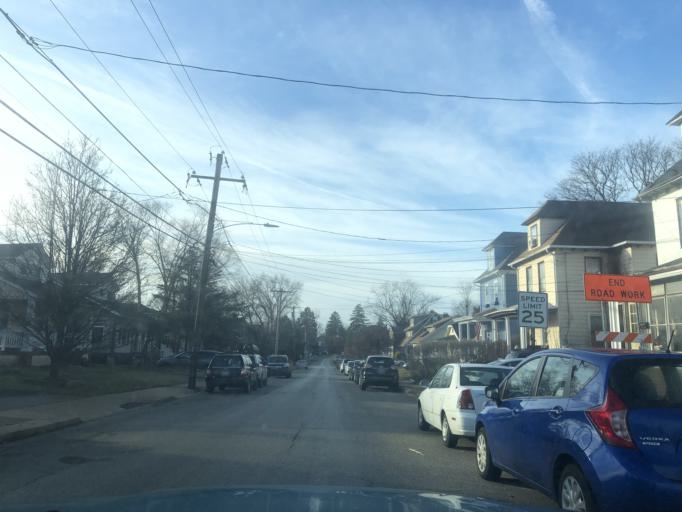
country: US
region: Pennsylvania
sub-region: Montgomery County
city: Glenside
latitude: 40.1128
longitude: -75.1531
